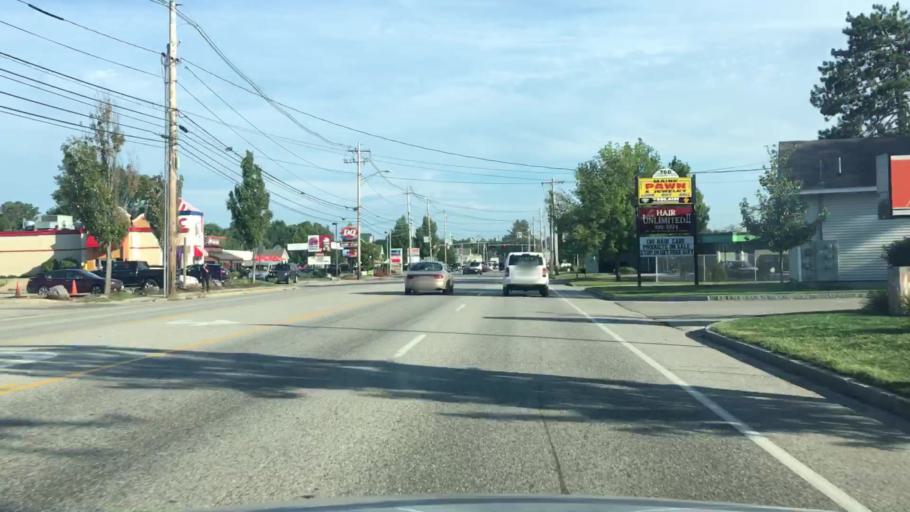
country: US
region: Maine
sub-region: Cumberland County
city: North Windham
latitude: 43.8359
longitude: -70.4399
